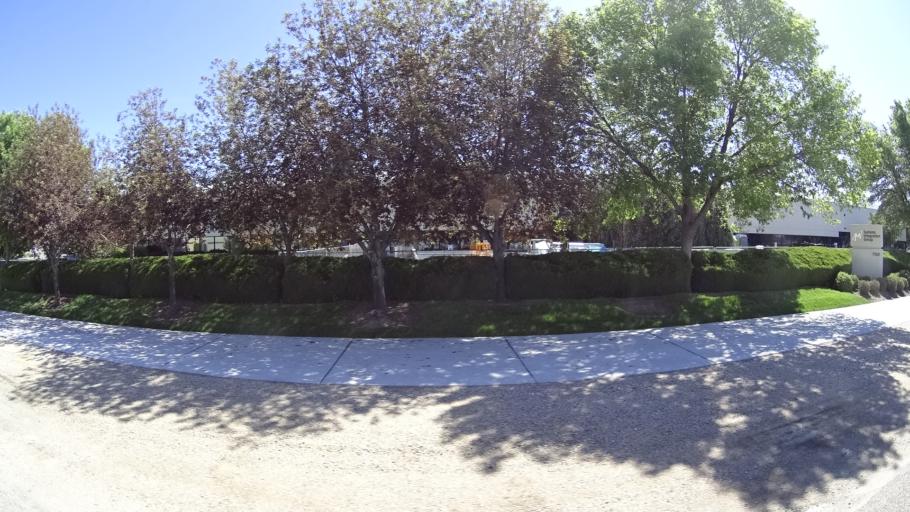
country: US
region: Idaho
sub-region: Ada County
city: Boise
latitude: 43.5330
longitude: -116.1521
